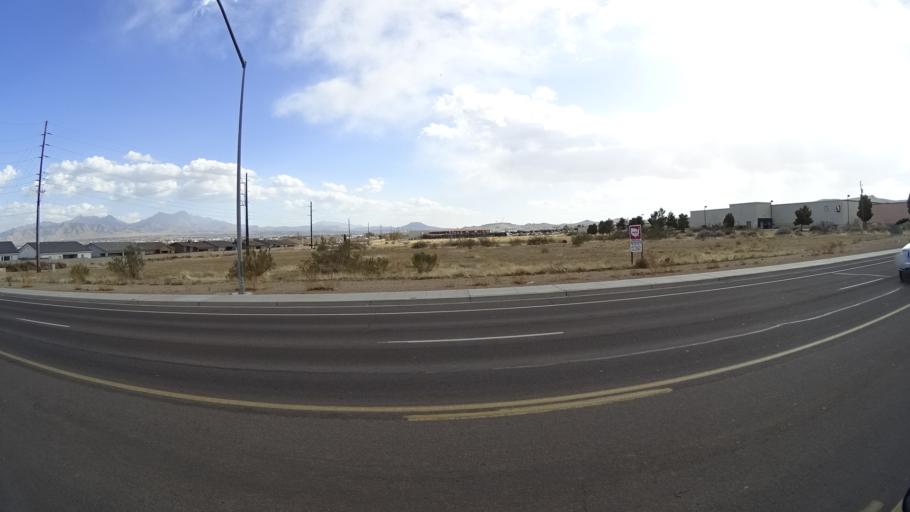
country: US
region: Arizona
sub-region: Mohave County
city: New Kingman-Butler
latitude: 35.2395
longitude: -114.0344
